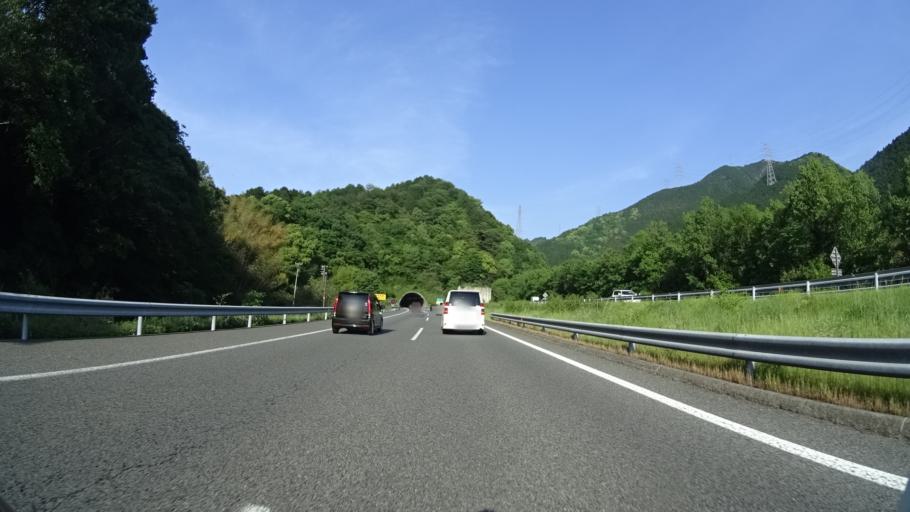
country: JP
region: Ehime
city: Saijo
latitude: 33.8847
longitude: 133.1875
